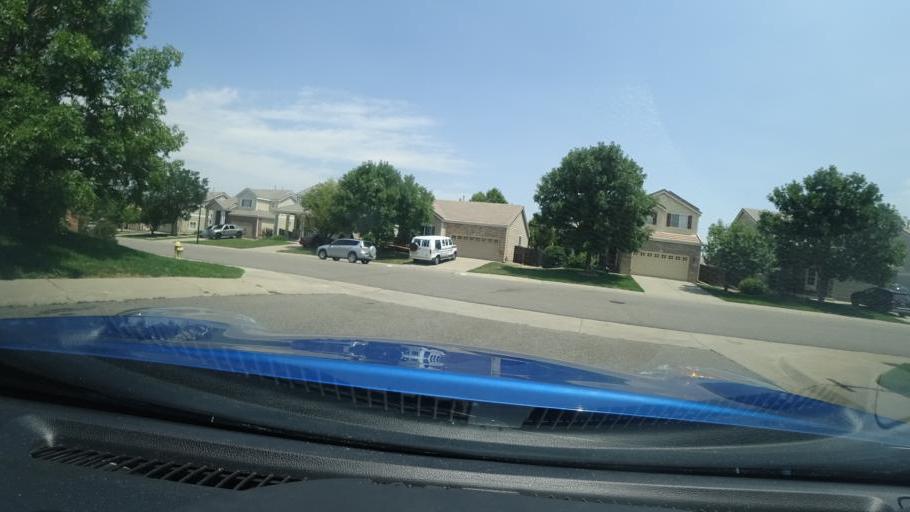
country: US
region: Colorado
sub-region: Adams County
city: Aurora
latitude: 39.6734
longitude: -104.7562
